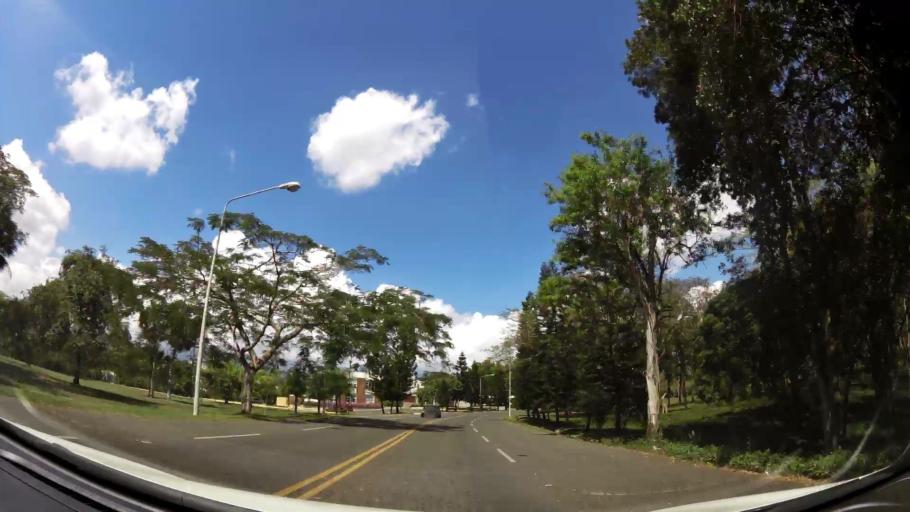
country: DO
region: Santiago
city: Santiago de los Caballeros
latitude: 19.4464
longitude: -70.6849
